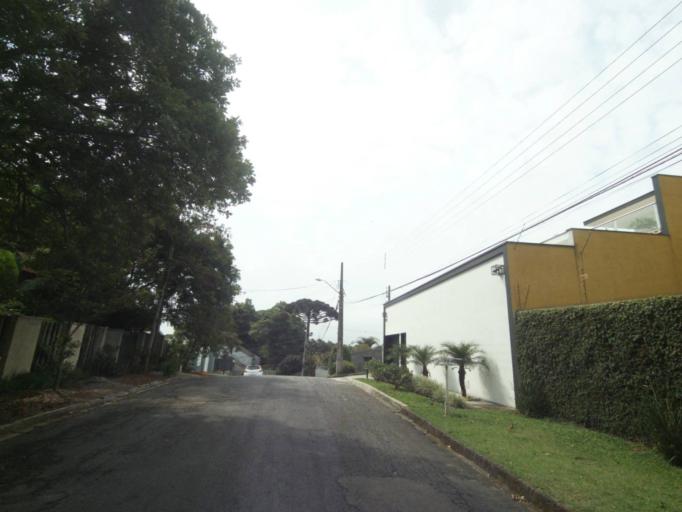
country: BR
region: Parana
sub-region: Curitiba
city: Curitiba
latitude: -25.4047
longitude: -49.2954
